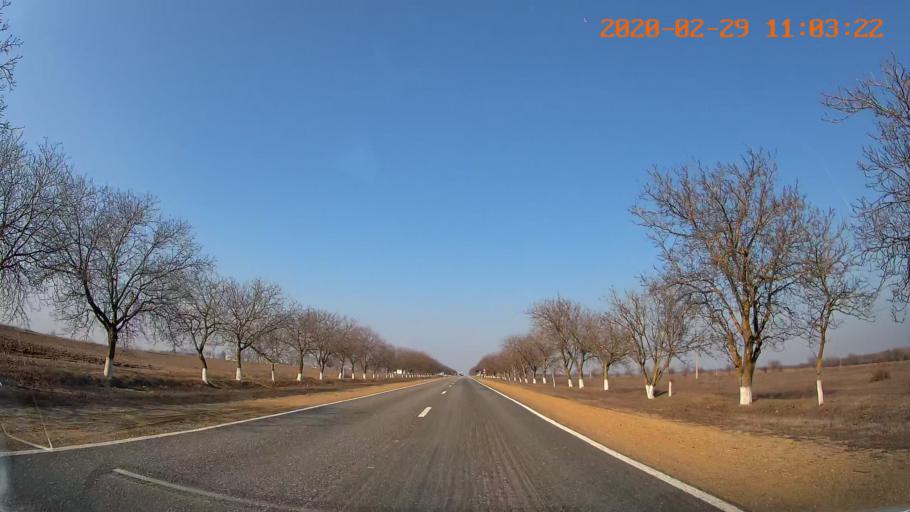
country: MD
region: Criuleni
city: Criuleni
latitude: 47.1791
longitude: 29.2189
